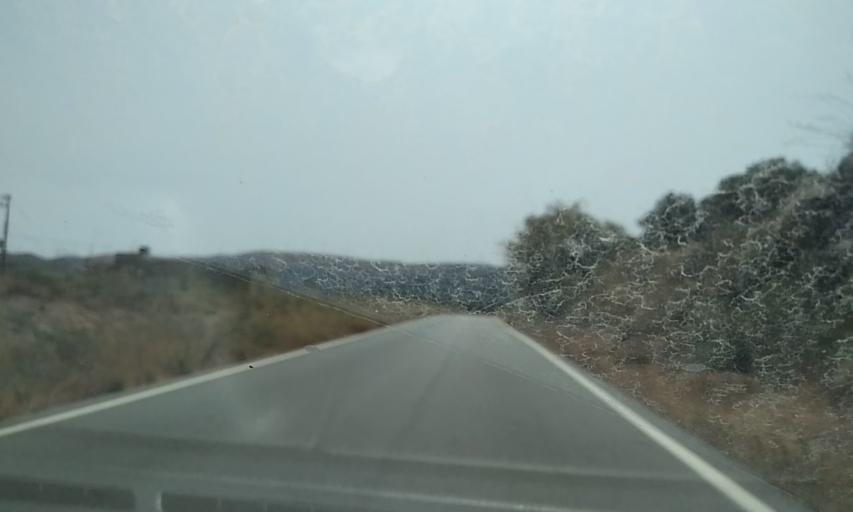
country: GR
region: Crete
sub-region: Nomos Lasithiou
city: Siteia
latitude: 35.1188
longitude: 26.0619
